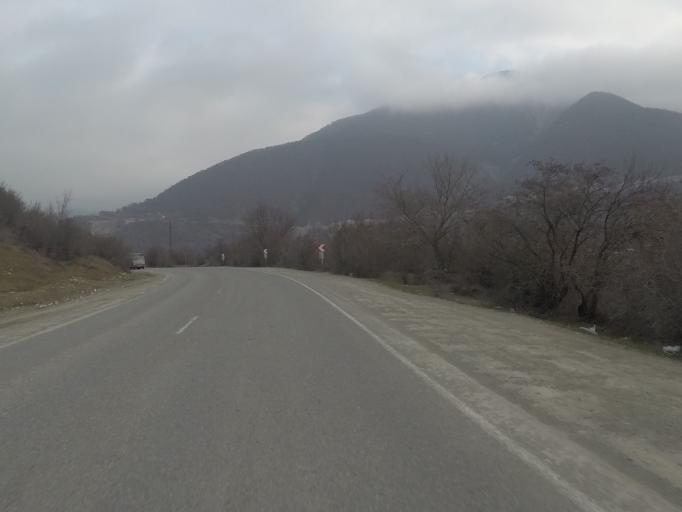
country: GE
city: Zhinvali
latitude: 42.1209
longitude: 44.7761
